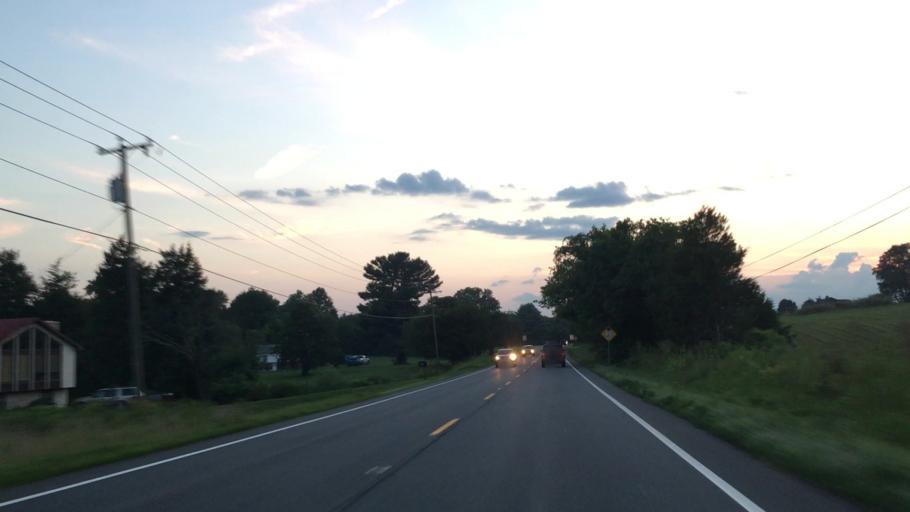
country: US
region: Virginia
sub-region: Orange County
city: Orange
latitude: 38.2436
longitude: -78.0698
